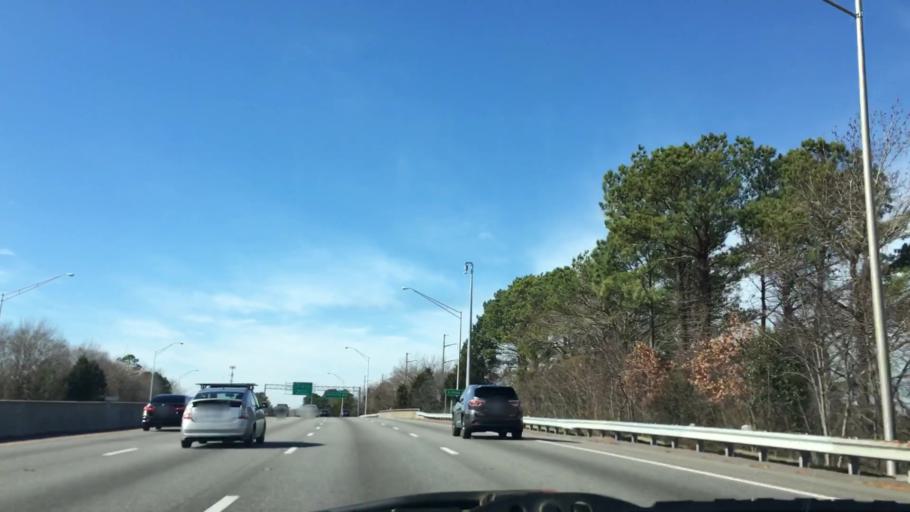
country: US
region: Virginia
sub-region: City of Virginia Beach
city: Virginia Beach
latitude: 36.8360
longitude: -76.0886
